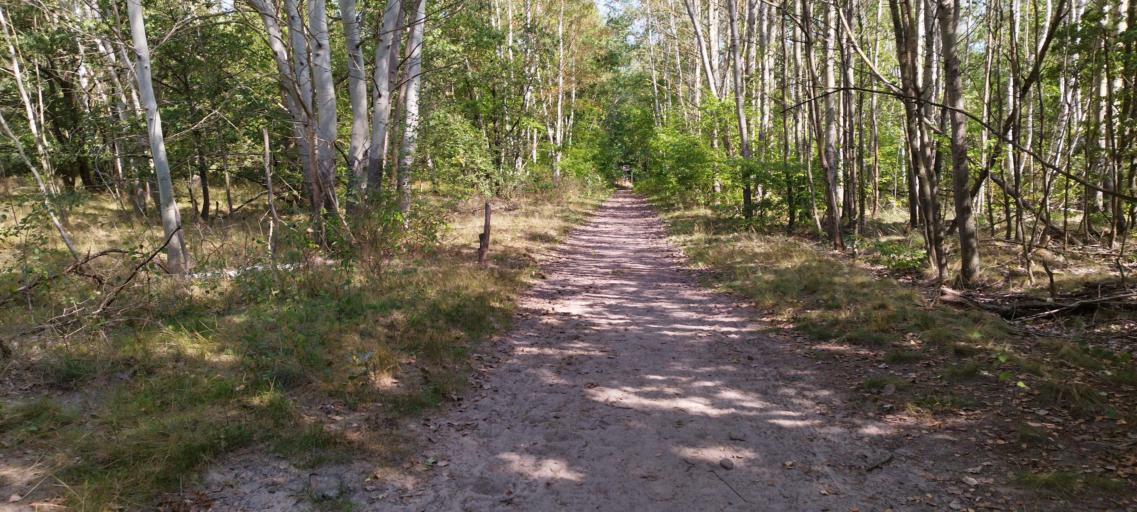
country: DE
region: Brandenburg
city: Dallgow-Doeberitz
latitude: 52.5317
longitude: 13.0734
